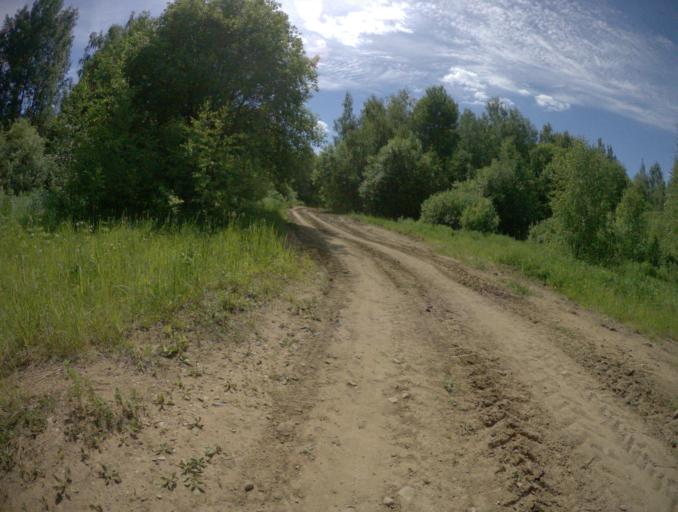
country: RU
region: Vladimir
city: Stavrovo
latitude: 56.3199
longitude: 40.0853
